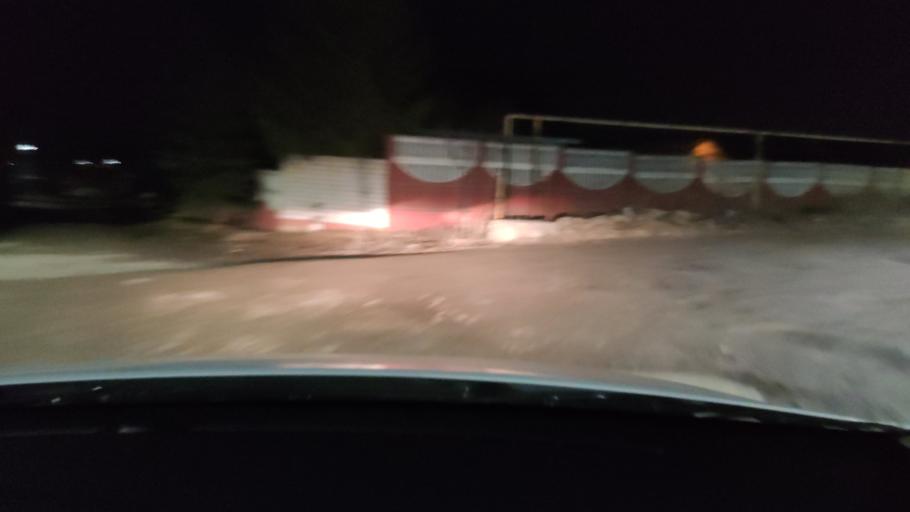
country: RU
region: Tatarstan
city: Vysokaya Gora
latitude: 55.8531
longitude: 49.2380
